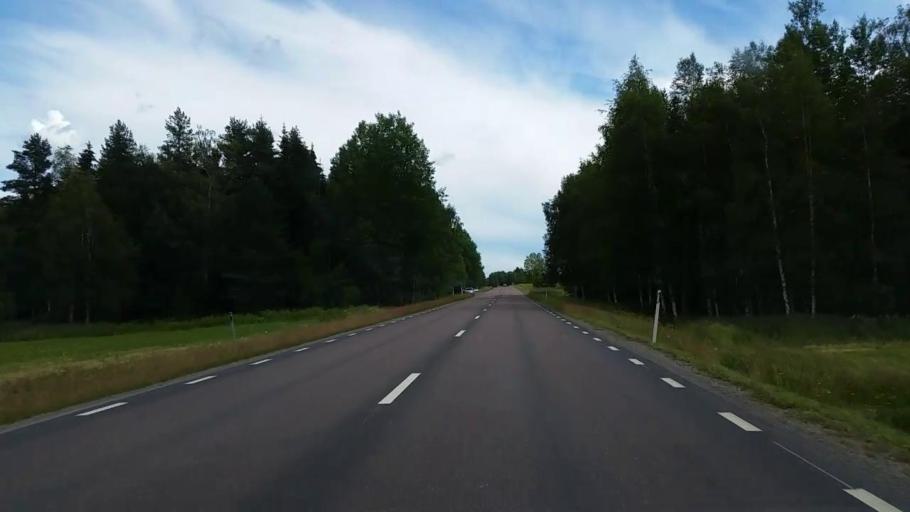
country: SE
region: Gaevleborg
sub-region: Ovanakers Kommun
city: Edsbyn
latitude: 61.3685
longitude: 15.8645
